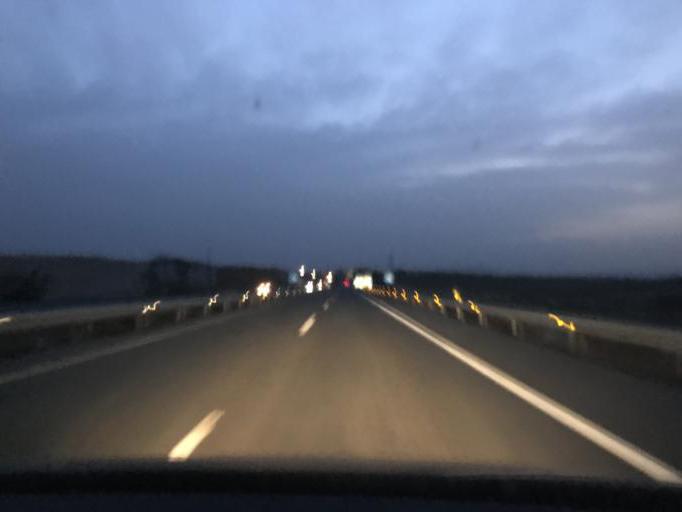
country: ES
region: Andalusia
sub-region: Provincia de Granada
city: Gor
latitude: 37.3967
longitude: -2.9797
